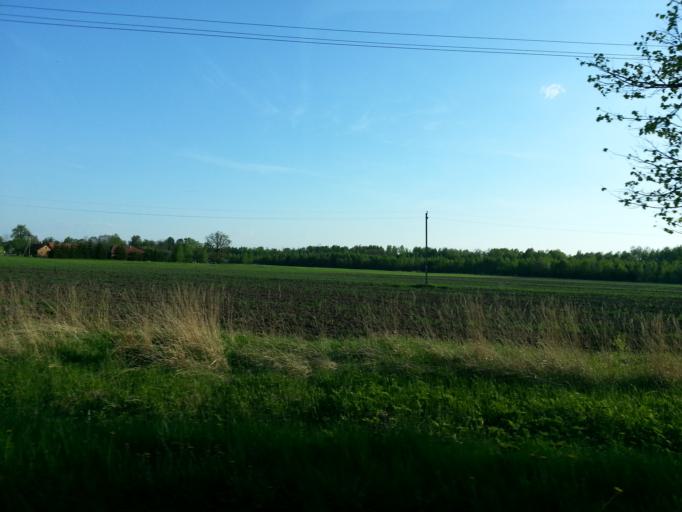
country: LT
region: Vilnius County
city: Ukmerge
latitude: 55.4230
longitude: 24.5625
